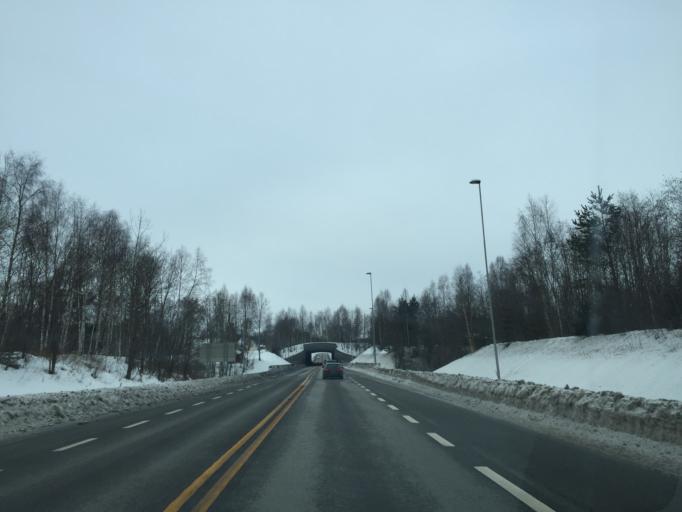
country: NO
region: Hedmark
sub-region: Loten
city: Loten
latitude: 60.7884
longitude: 11.3008
